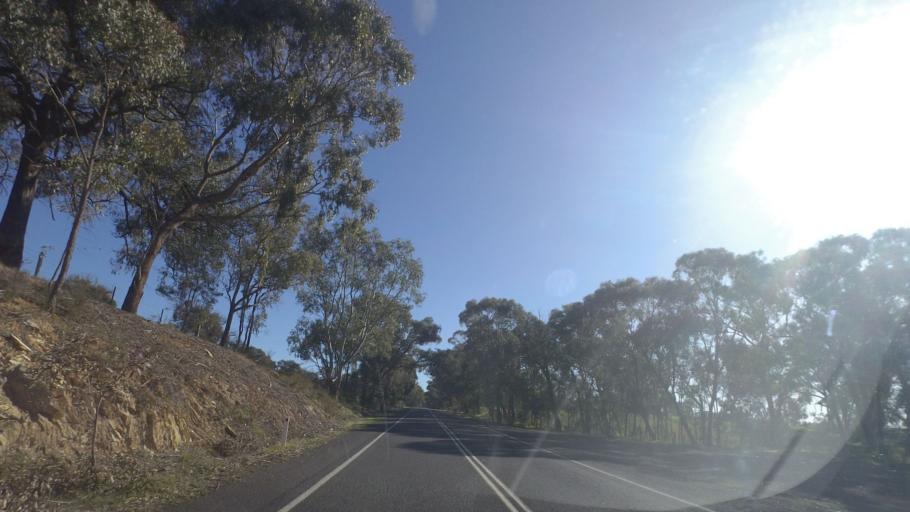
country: AU
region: Victoria
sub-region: Greater Bendigo
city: Kennington
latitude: -36.9207
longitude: 144.3425
